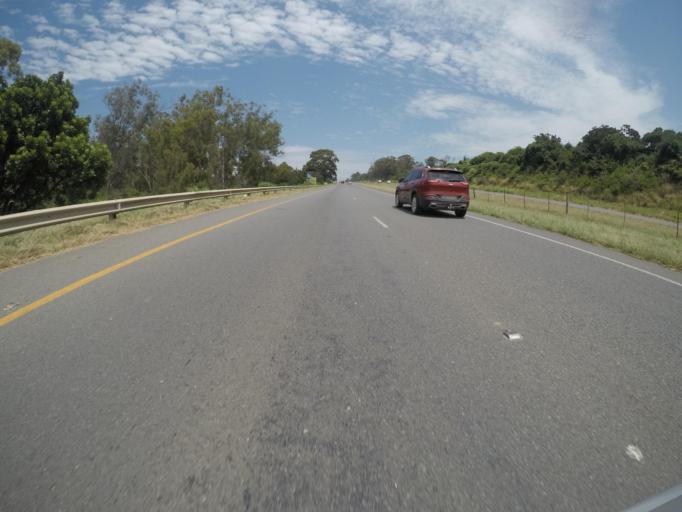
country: ZA
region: Eastern Cape
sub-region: Buffalo City Metropolitan Municipality
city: East London
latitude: -32.9471
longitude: 27.9399
